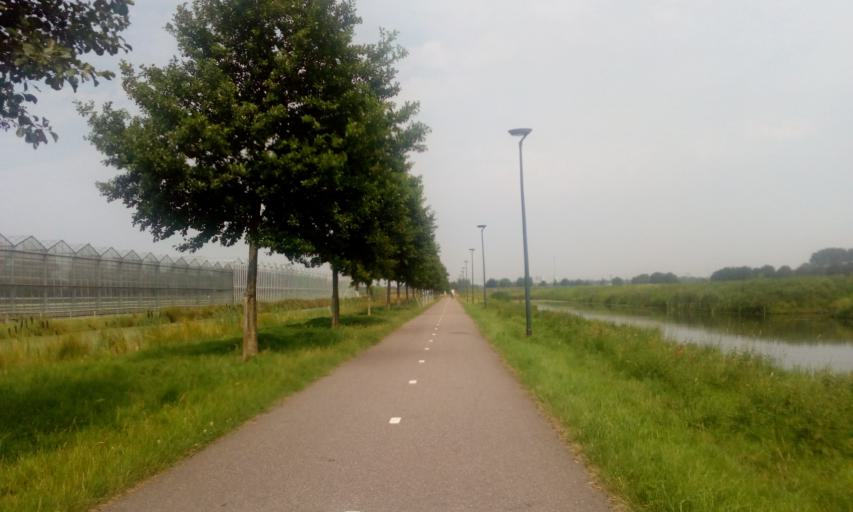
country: NL
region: South Holland
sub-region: Gemeente Krimpen aan den IJssel
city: Krimpen aan den IJssel
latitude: 51.9532
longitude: 4.6061
